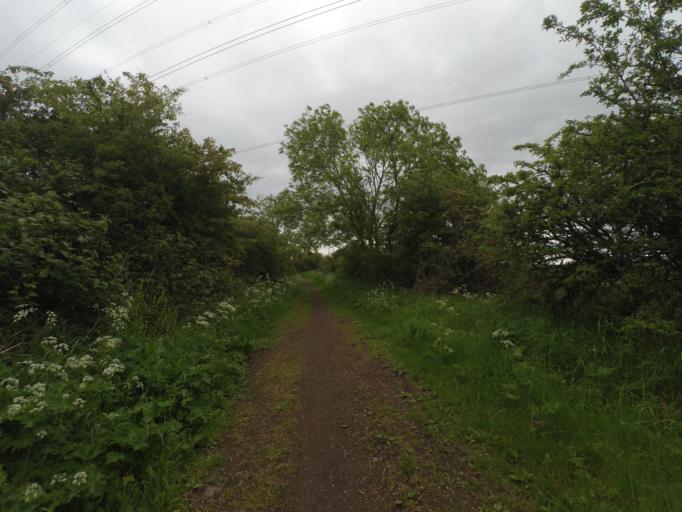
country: GB
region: Scotland
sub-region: East Lothian
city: Tranent
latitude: 55.9256
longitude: -2.9798
